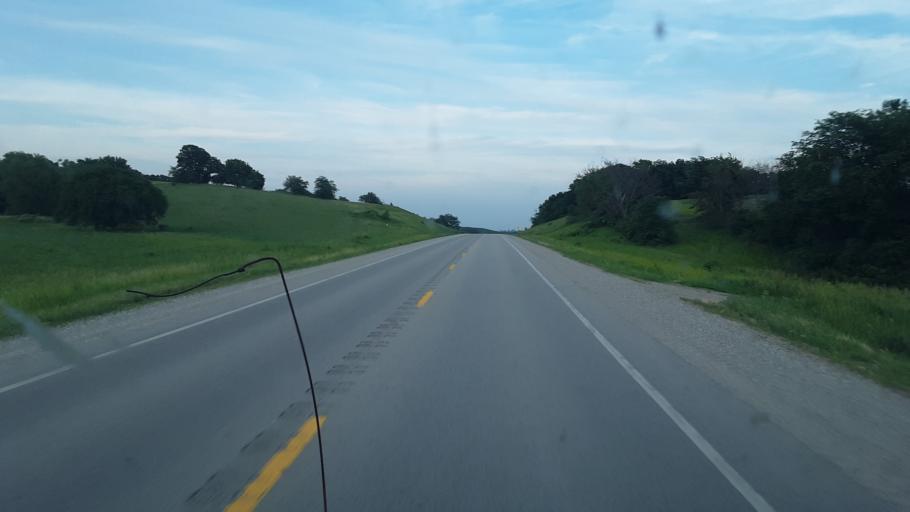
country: US
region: Iowa
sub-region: Benton County
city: Belle Plaine
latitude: 41.7428
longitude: -92.2630
